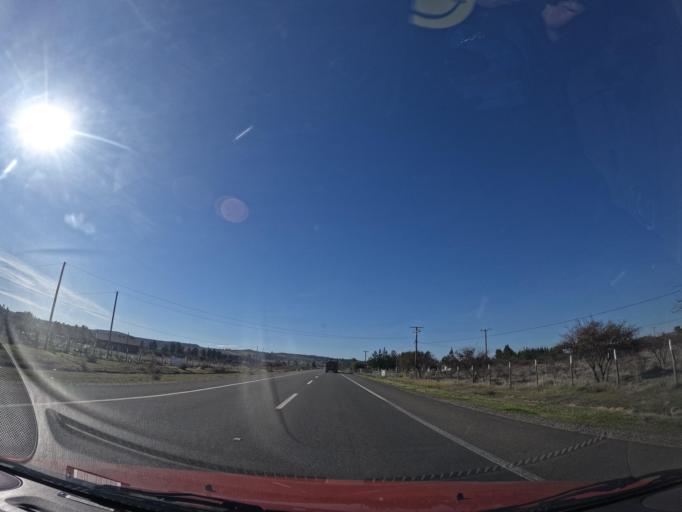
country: CL
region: Maule
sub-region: Provincia de Cauquenes
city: Cauquenes
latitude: -35.9520
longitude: -72.2079
